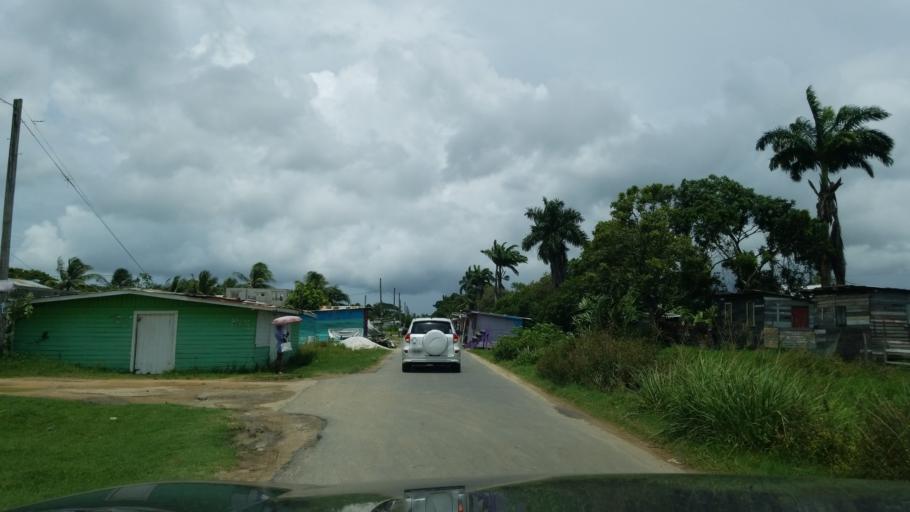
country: GY
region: Demerara-Mahaica
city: Georgetown
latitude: 6.7958
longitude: -58.1250
